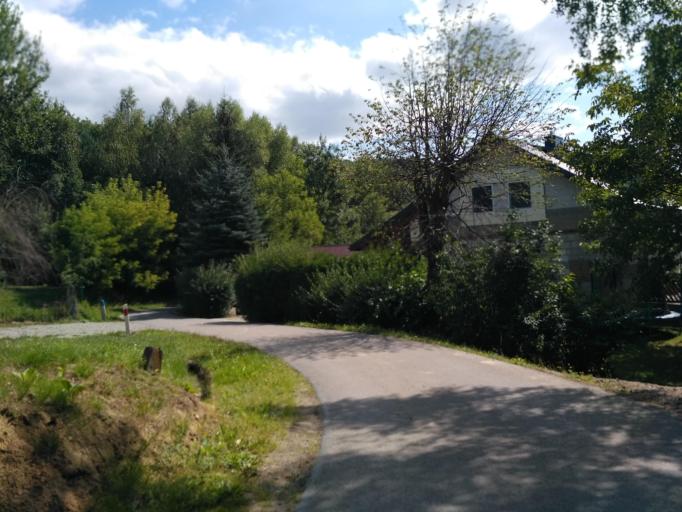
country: PL
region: Subcarpathian Voivodeship
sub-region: Powiat strzyzowski
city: Polomia
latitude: 49.9154
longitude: 21.8864
